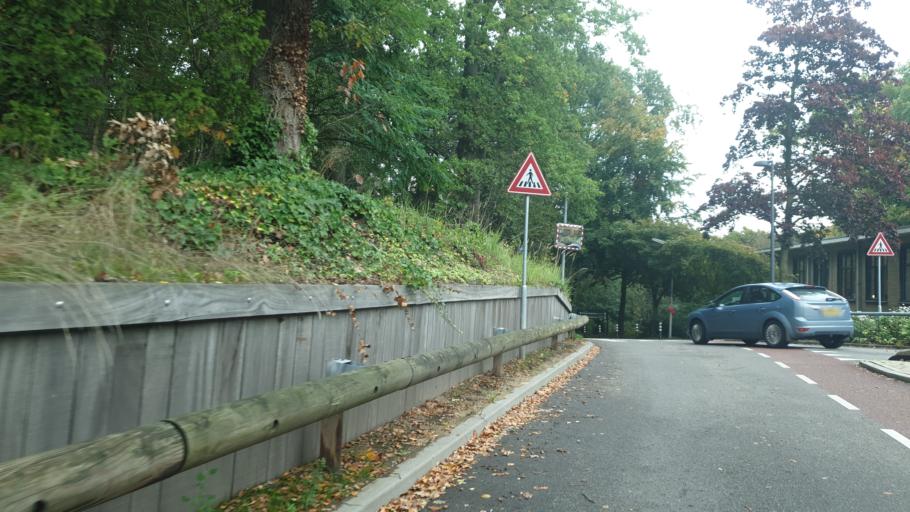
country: NL
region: Gelderland
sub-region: Gemeente Groesbeek
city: Berg en Dal
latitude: 51.8338
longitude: 5.8981
